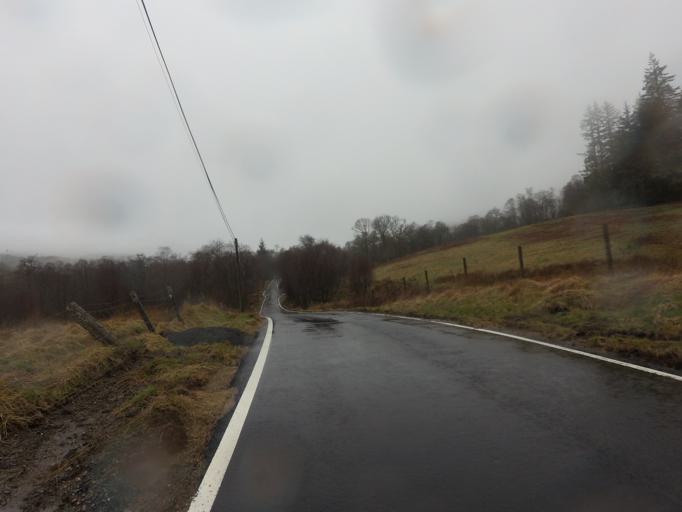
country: GB
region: Scotland
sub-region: West Dunbartonshire
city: Balloch
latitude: 56.1952
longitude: -4.5172
